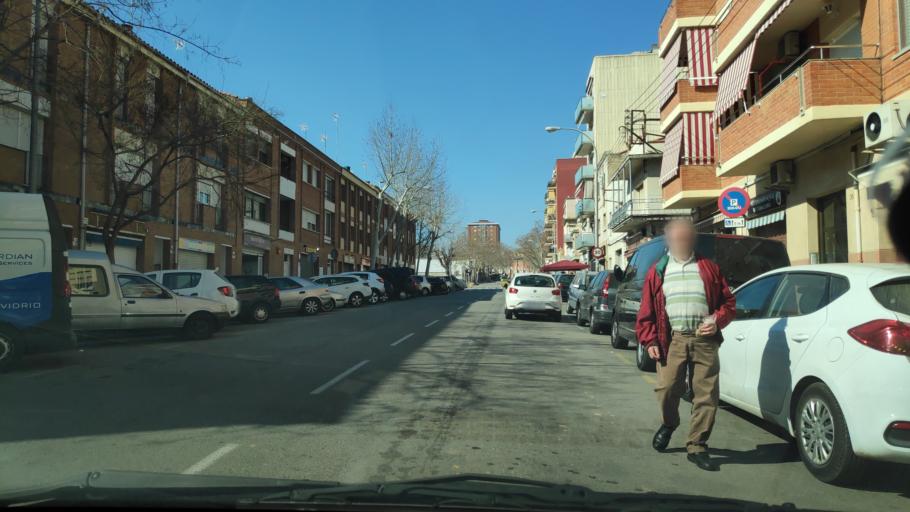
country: ES
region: Catalonia
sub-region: Provincia de Barcelona
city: Sant Quirze del Valles
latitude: 41.5453
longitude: 2.0868
